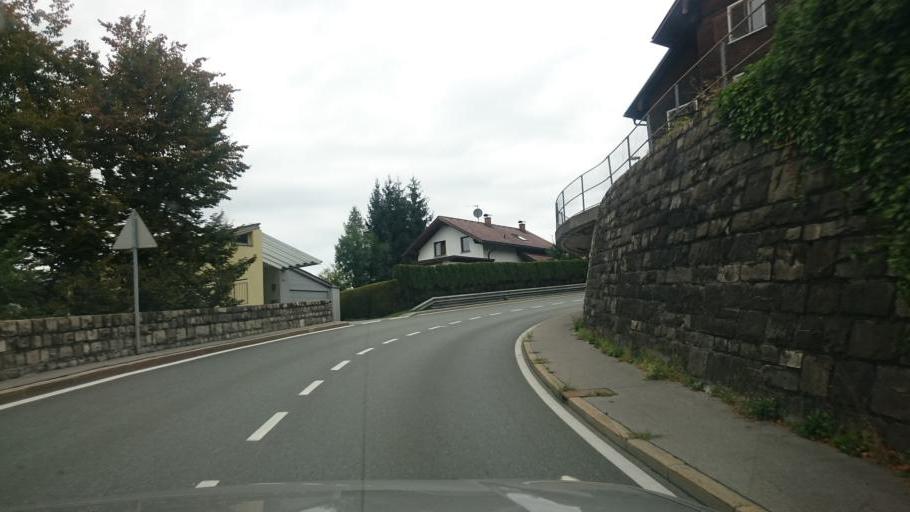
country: AT
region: Vorarlberg
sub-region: Politischer Bezirk Dornbirn
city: Dornbirn
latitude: 47.4104
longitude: 9.7554
